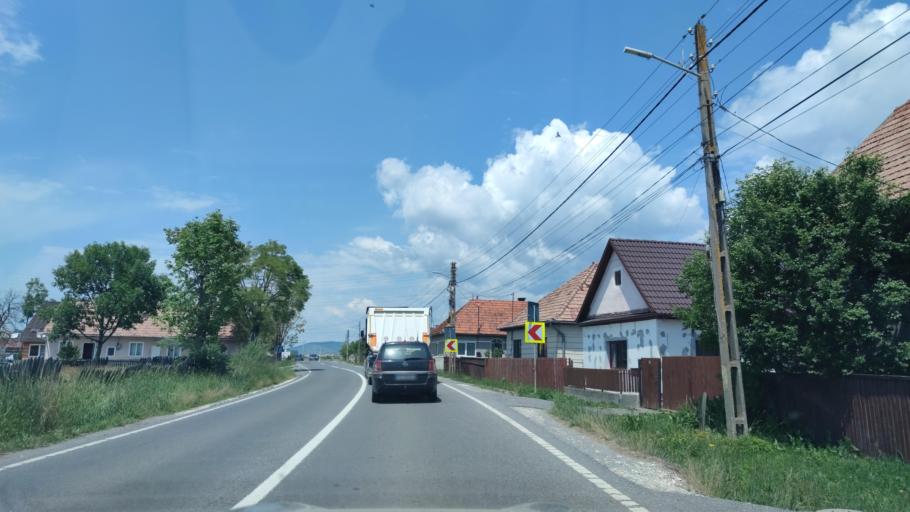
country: RO
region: Harghita
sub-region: Comuna Suseni
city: Valea Stramba
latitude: 46.6988
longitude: 25.5998
